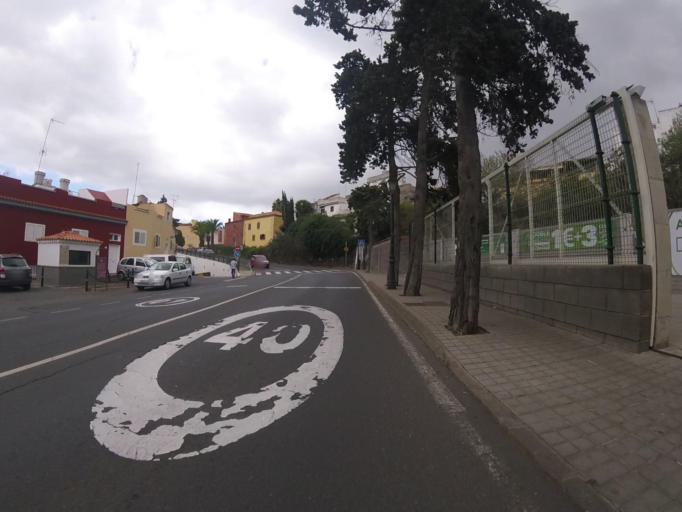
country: ES
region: Canary Islands
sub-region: Provincia de Las Palmas
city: Vega de San Mateo
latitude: 28.0089
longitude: -15.5356
